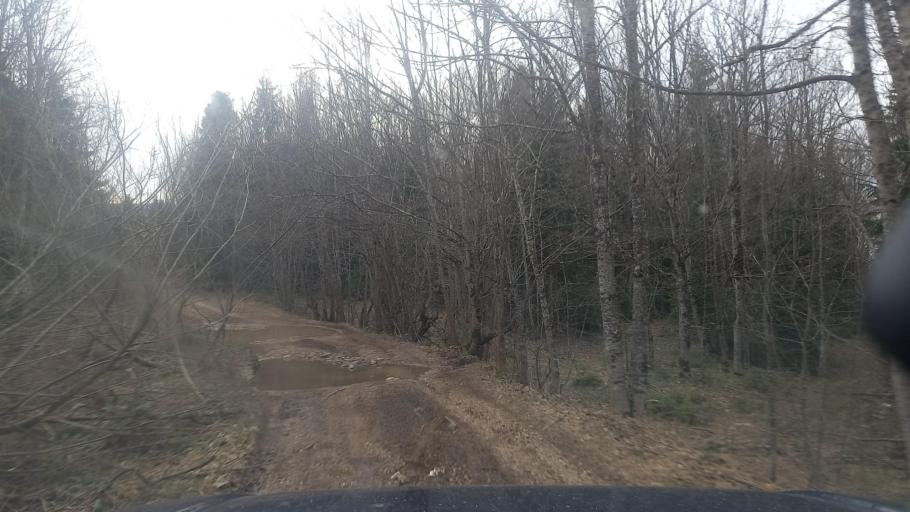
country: RU
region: Adygeya
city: Kamennomostskiy
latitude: 44.1866
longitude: 39.9906
